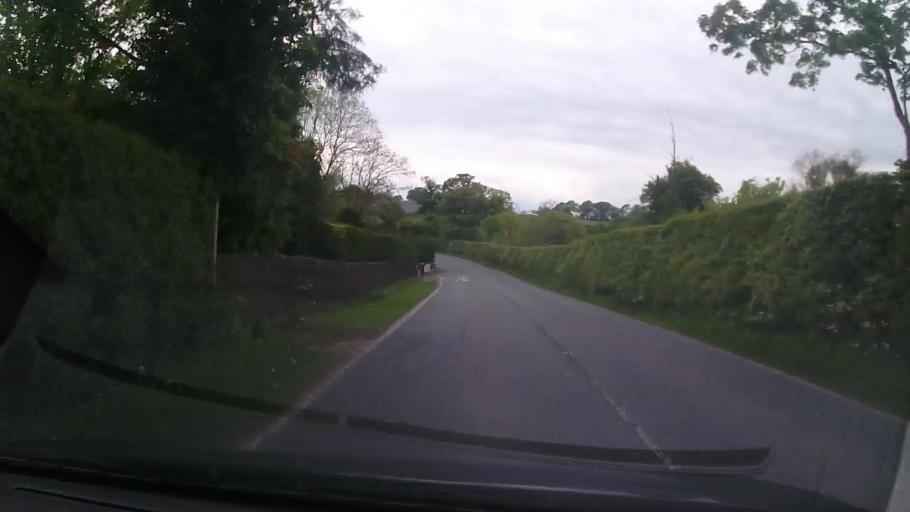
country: GB
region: Wales
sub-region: Wrexham
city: Overton
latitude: 52.9632
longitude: -2.9168
